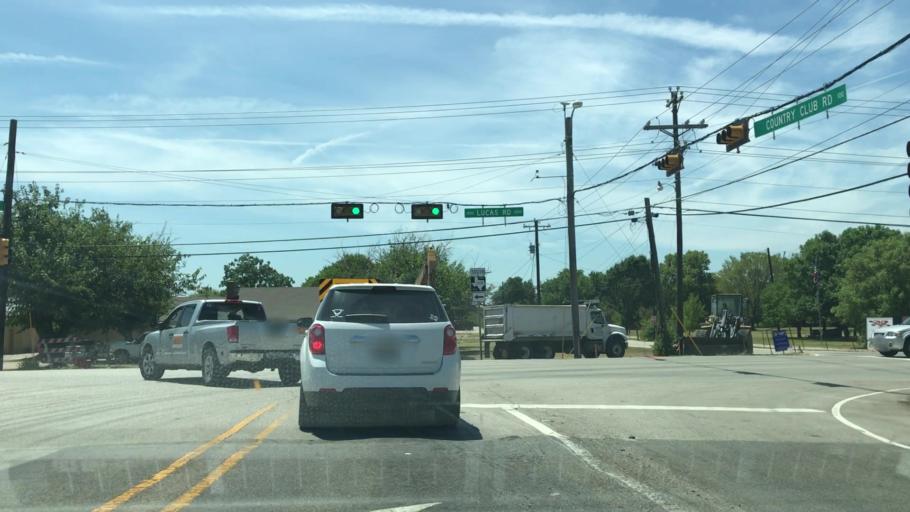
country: US
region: Texas
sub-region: Collin County
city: Lucas
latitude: 33.0855
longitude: -96.5909
